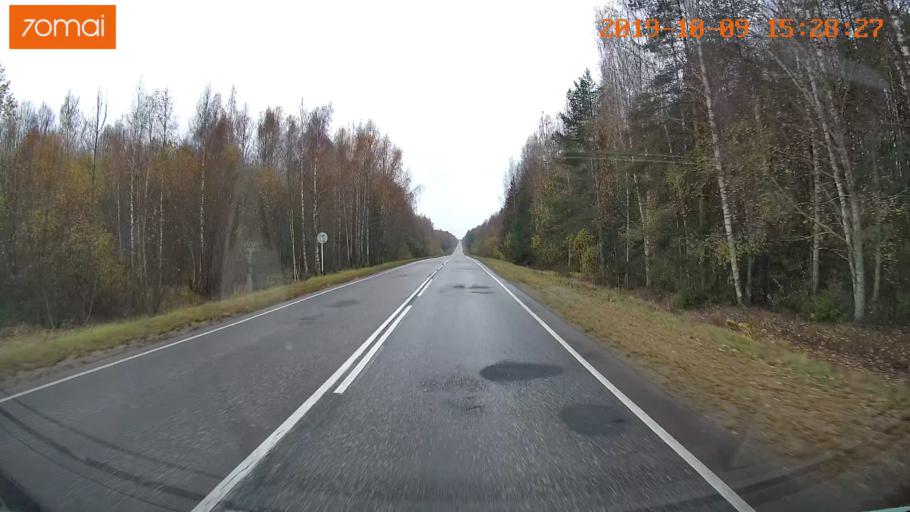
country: RU
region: Kostroma
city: Susanino
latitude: 58.0030
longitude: 41.3598
